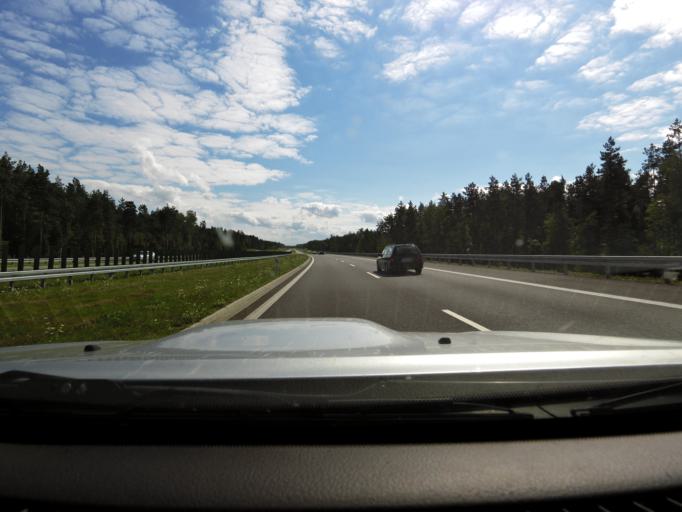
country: PL
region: Warmian-Masurian Voivodeship
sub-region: Powiat ostrodzki
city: Milomlyn
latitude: 53.7602
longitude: 19.8578
